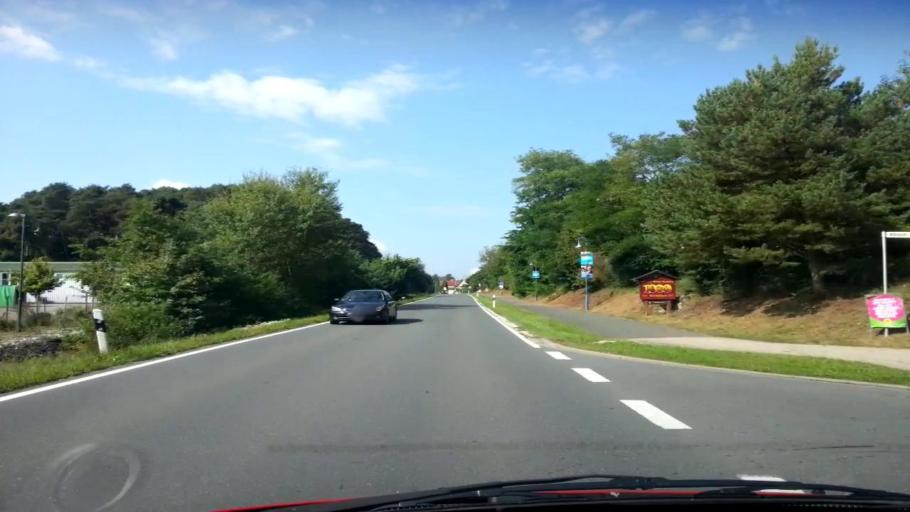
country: DE
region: Bavaria
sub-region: Upper Franconia
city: Heroldsbach
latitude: 49.6918
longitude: 11.0129
